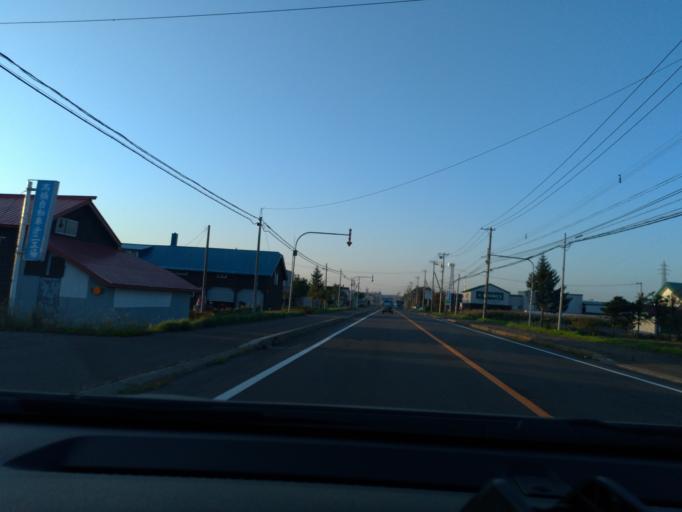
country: JP
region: Hokkaido
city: Tobetsu
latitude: 43.2058
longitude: 141.5201
